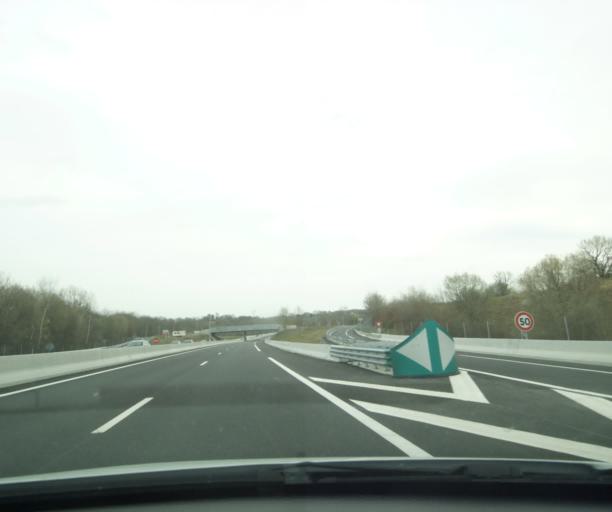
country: FR
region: Aquitaine
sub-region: Departement des Pyrenees-Atlantiques
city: Lahonce
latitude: 43.4518
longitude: -1.3840
